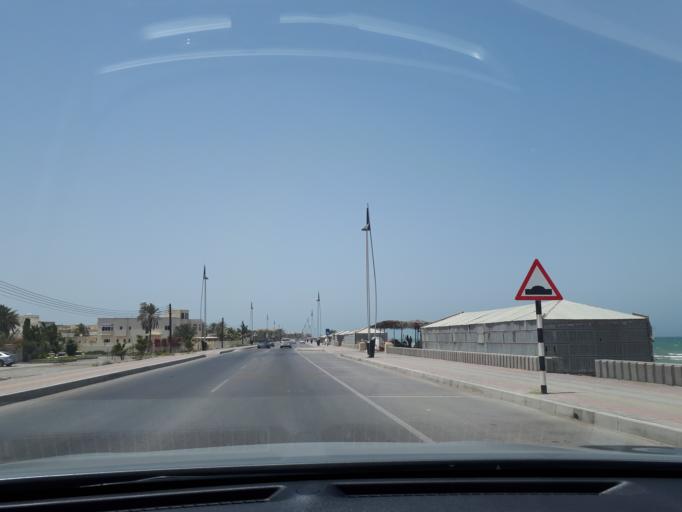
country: OM
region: Muhafazat Masqat
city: As Sib al Jadidah
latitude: 23.6634
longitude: 58.2168
